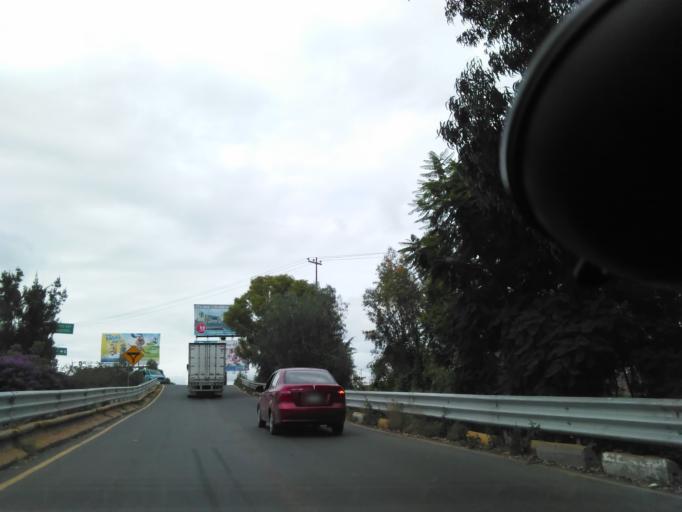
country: MX
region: Mexico
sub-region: Huehuetoca
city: Jorobas
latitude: 19.8252
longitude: -99.2479
